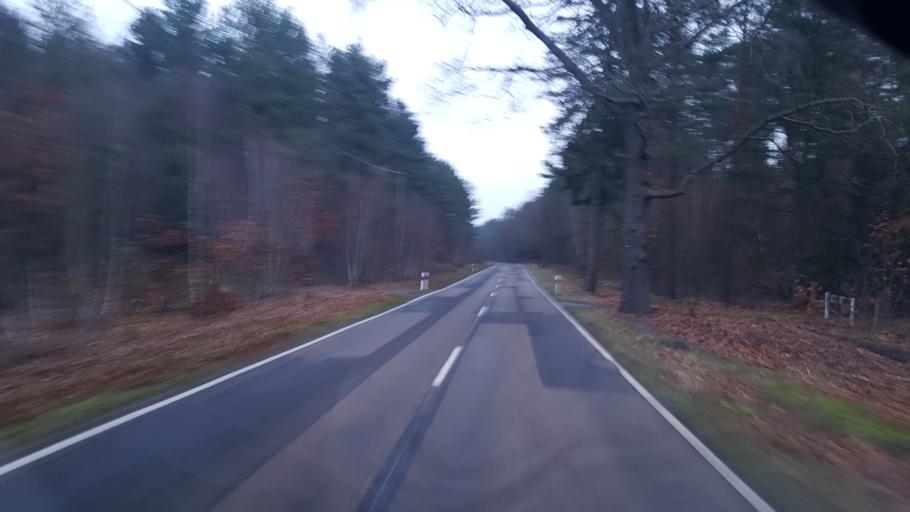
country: DE
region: Brandenburg
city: Drachhausen
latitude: 51.8757
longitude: 14.2882
